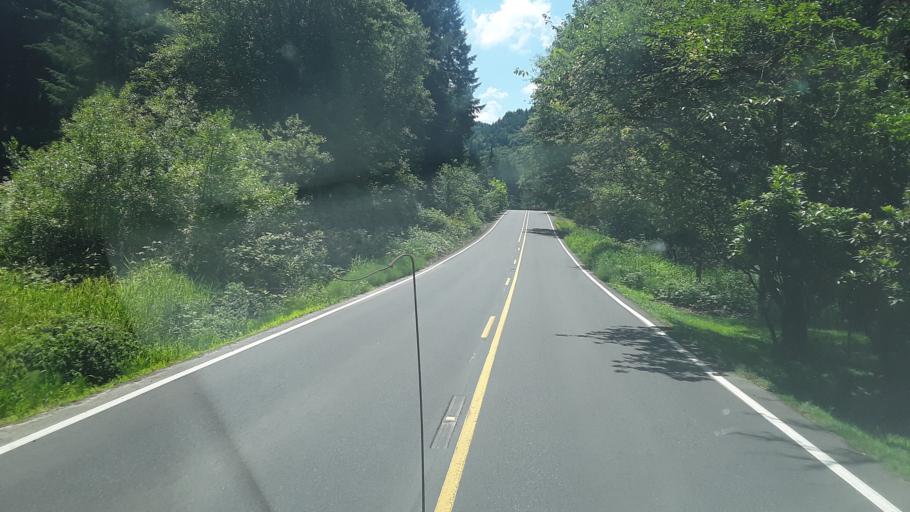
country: US
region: Washington
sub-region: Clark County
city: Yacolt
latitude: 45.9305
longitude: -122.3797
